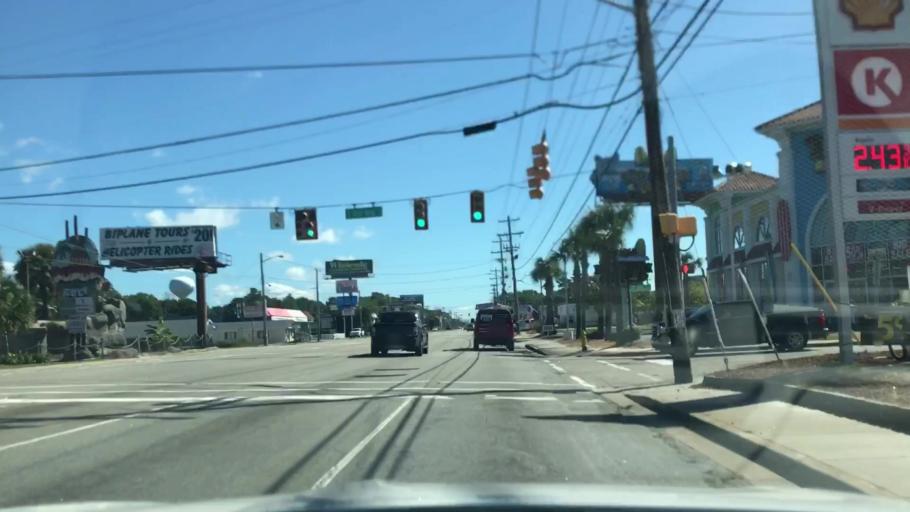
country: US
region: South Carolina
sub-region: Horry County
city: North Myrtle Beach
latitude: 33.8044
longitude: -78.7218
